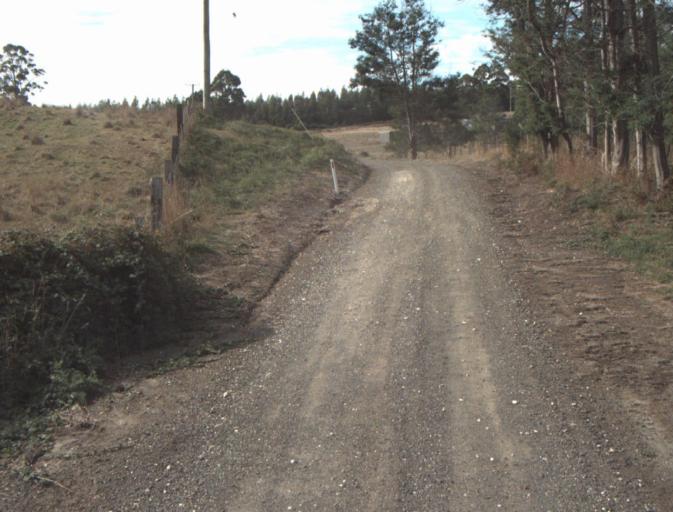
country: AU
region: Tasmania
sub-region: Launceston
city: Mayfield
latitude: -41.1966
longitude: 147.1946
